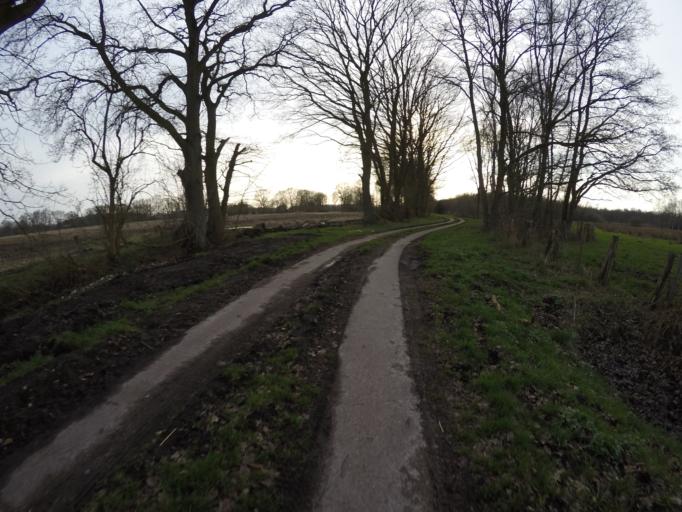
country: DE
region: Schleswig-Holstein
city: Hemdingen
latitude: 53.7281
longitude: 9.8582
